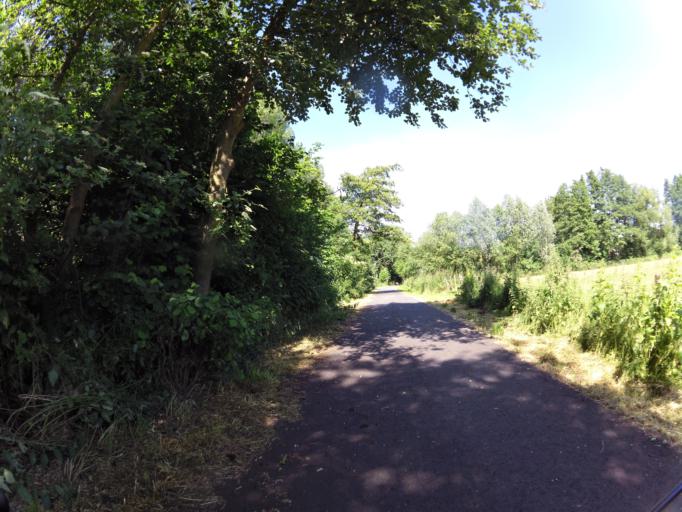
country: DE
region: North Rhine-Westphalia
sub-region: Regierungsbezirk Koln
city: Selfkant
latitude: 51.0061
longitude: 5.9030
